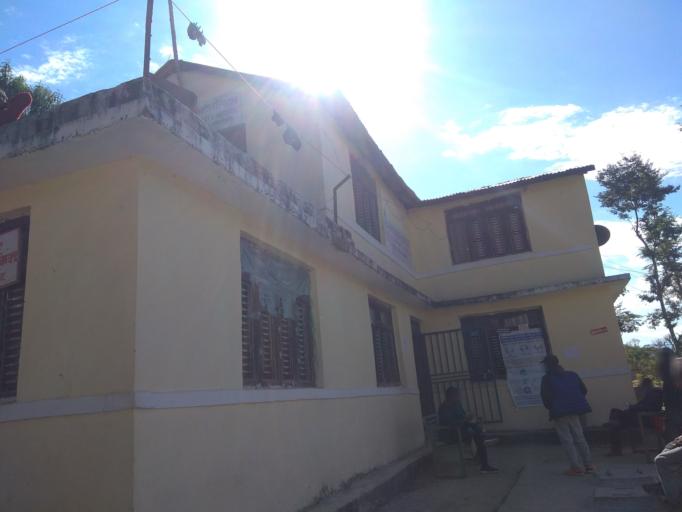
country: NP
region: Far Western
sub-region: Seti Zone
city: Achham
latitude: 29.2405
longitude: 81.6363
